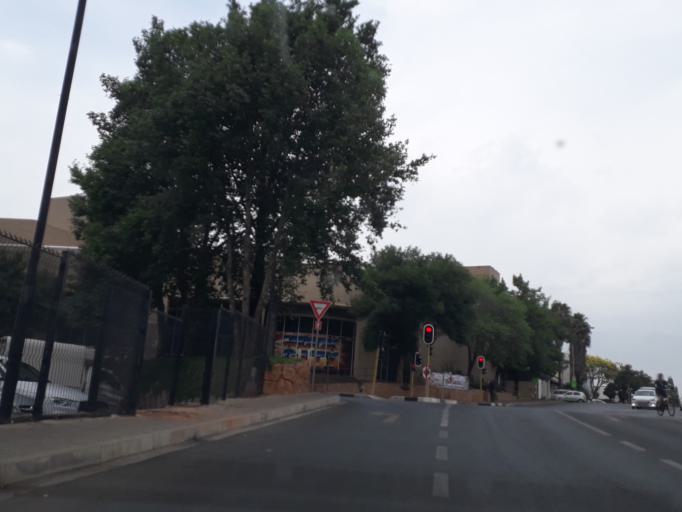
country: ZA
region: Gauteng
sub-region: City of Johannesburg Metropolitan Municipality
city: Johannesburg
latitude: -26.1320
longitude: 27.9750
